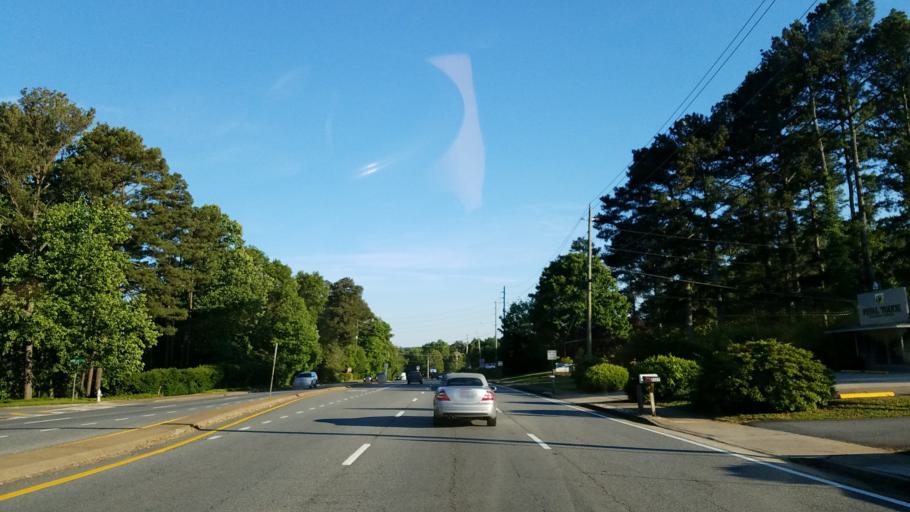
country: US
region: Georgia
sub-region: Cherokee County
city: Woodstock
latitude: 34.0836
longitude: -84.5753
